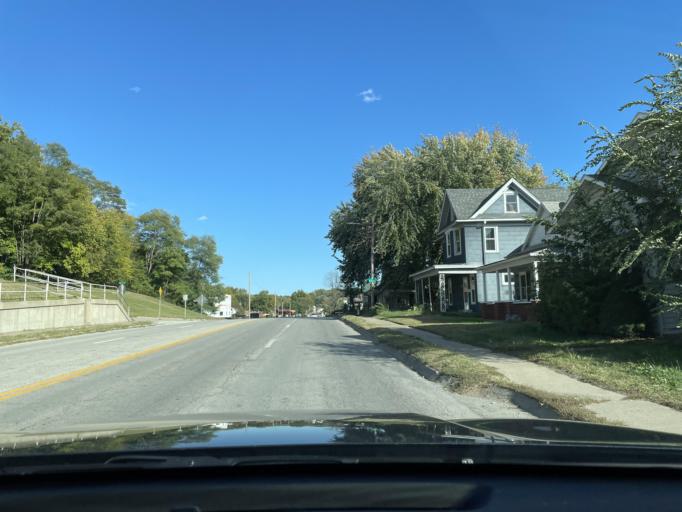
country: US
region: Kansas
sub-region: Doniphan County
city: Elwood
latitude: 39.7116
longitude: -94.8594
